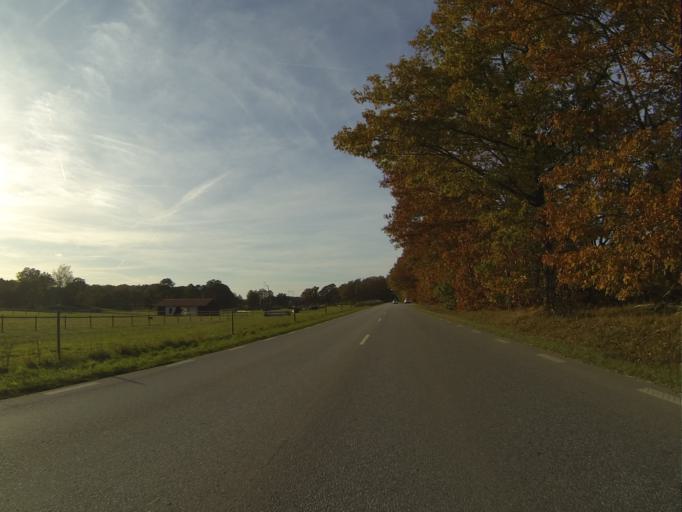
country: SE
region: Skane
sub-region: Hoors Kommun
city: Loberod
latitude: 55.7313
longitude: 13.4115
